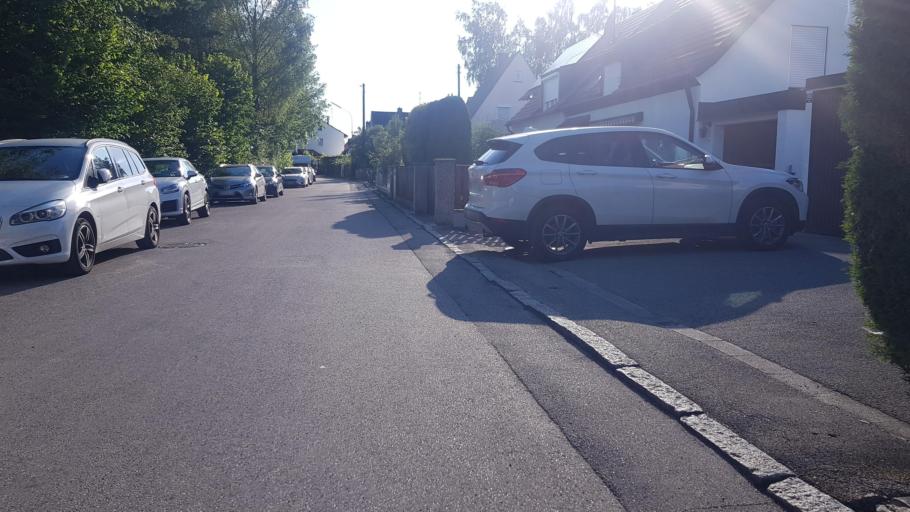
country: DE
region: Bavaria
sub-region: Upper Bavaria
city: Karlsfeld
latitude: 48.2436
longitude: 11.4844
